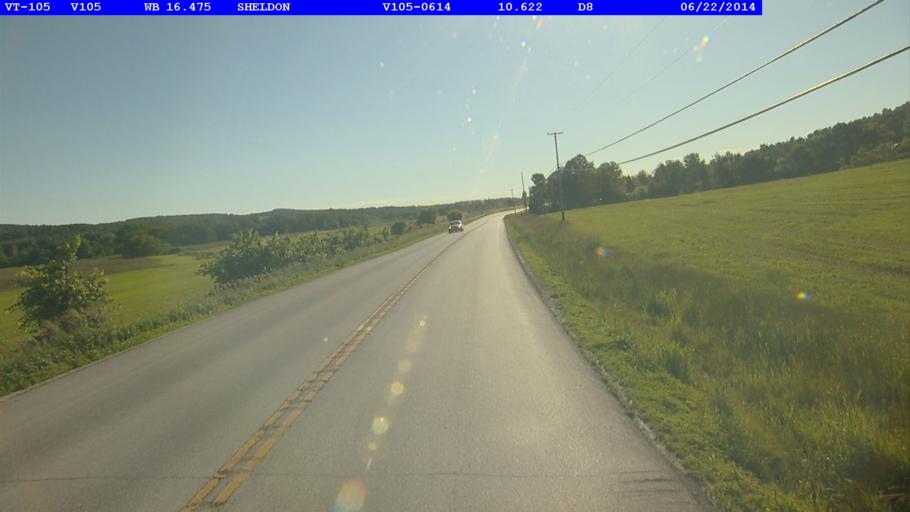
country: US
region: Vermont
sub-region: Franklin County
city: Enosburg Falls
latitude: 44.9073
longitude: -72.8276
